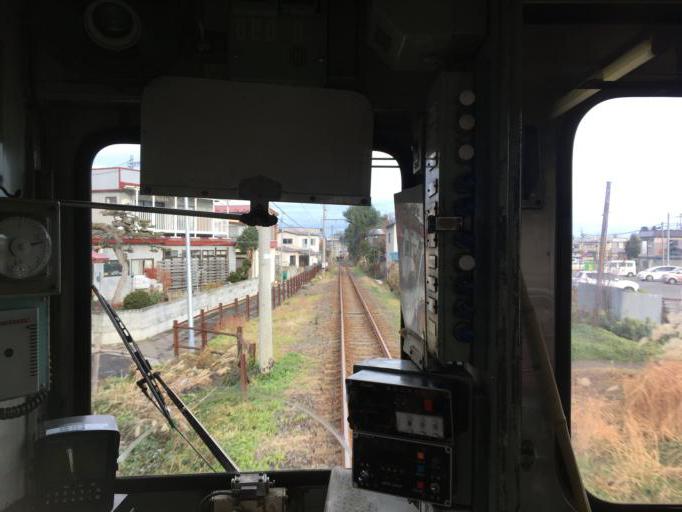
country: JP
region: Aomori
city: Hirosaki
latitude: 40.5867
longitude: 140.4697
